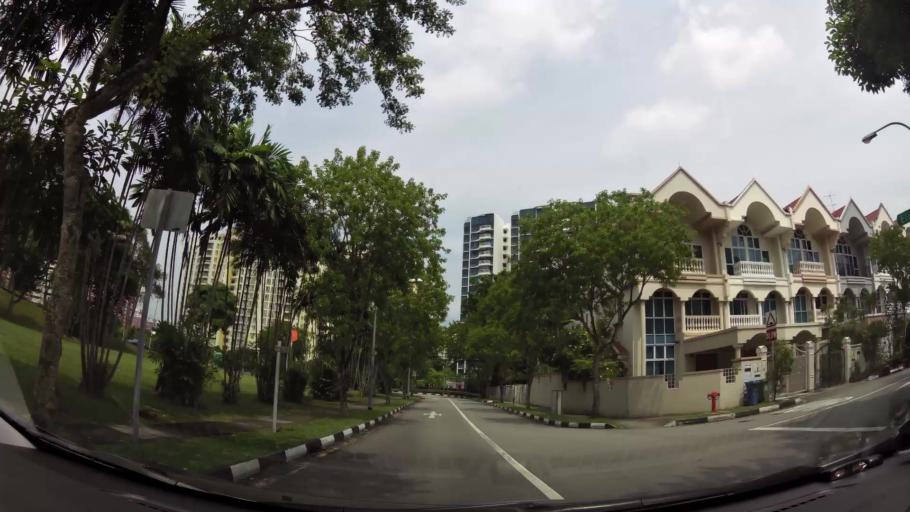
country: MY
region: Johor
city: Kampung Pasir Gudang Baru
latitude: 1.3722
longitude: 103.9406
